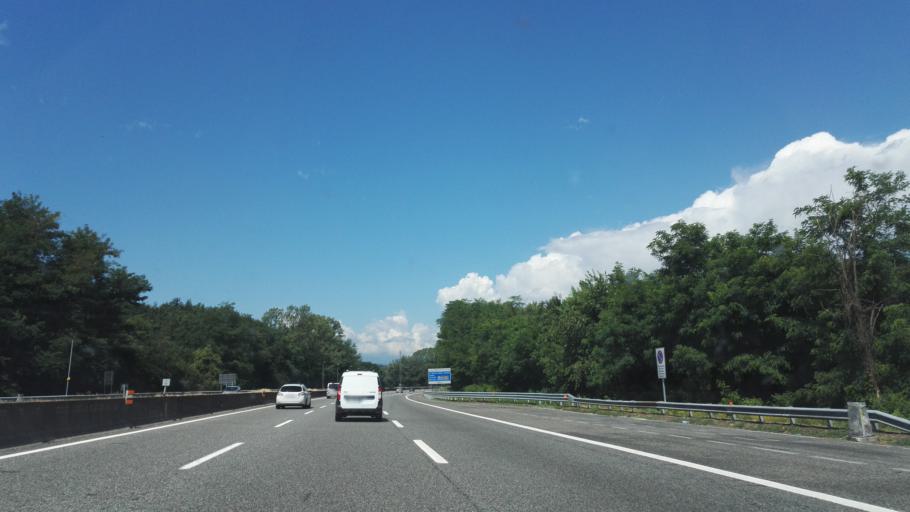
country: IT
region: Piedmont
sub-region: Provincia di Novara
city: Borgo Ticino
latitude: 45.6994
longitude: 8.6137
